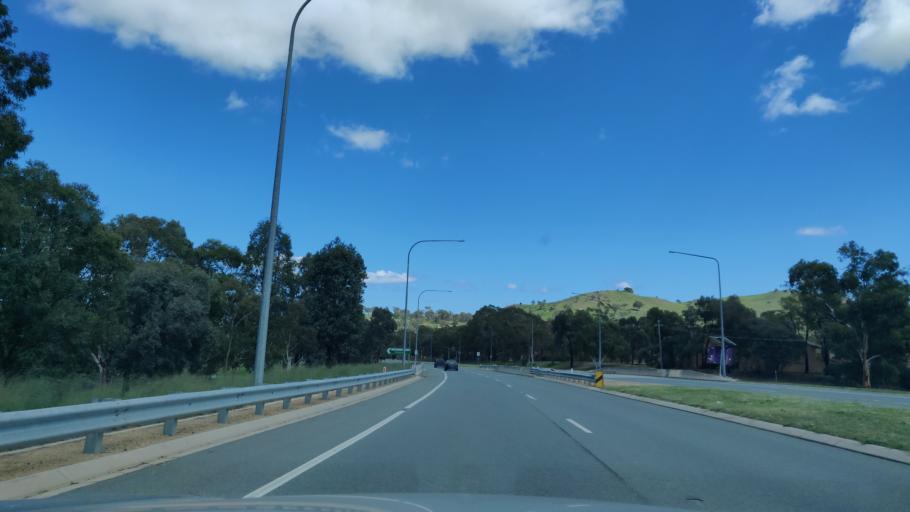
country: AU
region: Australian Capital Territory
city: Macarthur
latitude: -35.3975
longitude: 149.0695
